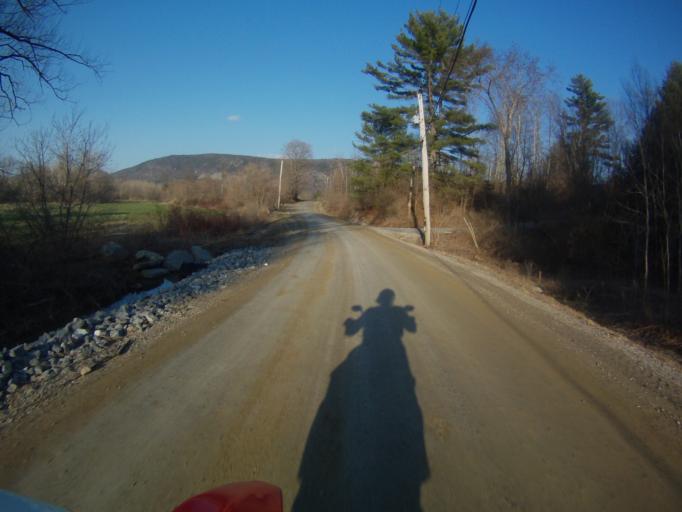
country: US
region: Vermont
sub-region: Addison County
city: Bristol
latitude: 44.0909
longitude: -73.1025
